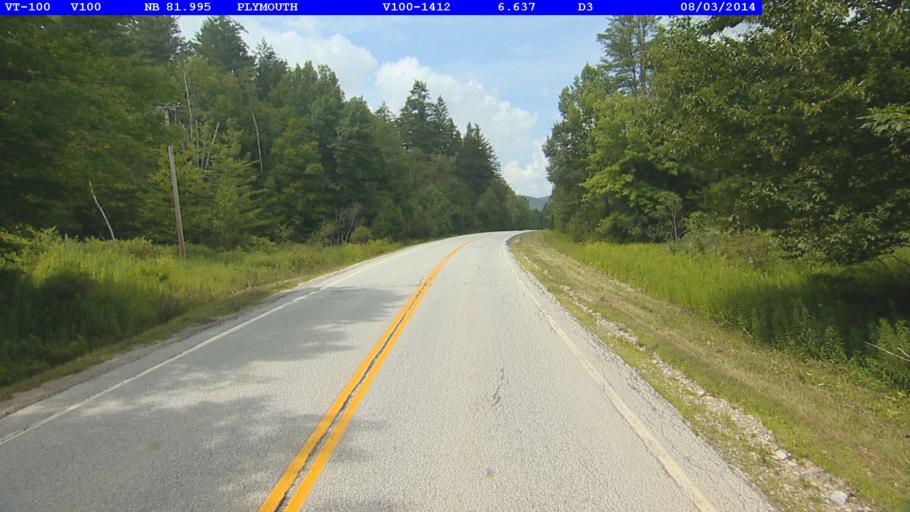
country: US
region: Vermont
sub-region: Rutland County
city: Rutland
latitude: 43.5463
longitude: -72.7515
